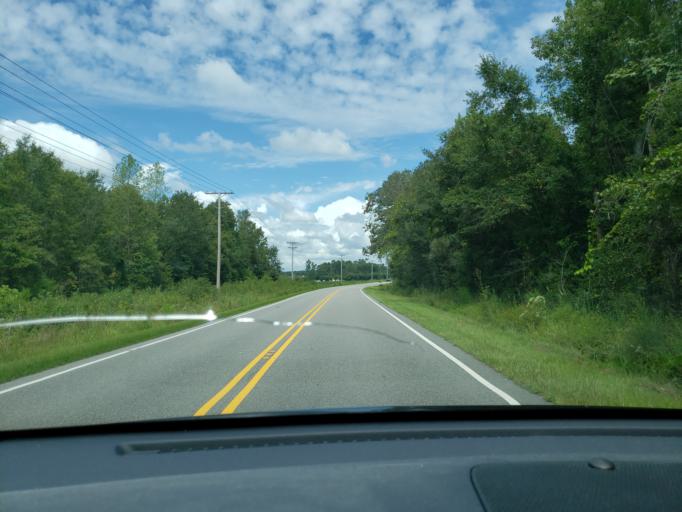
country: US
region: North Carolina
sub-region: Columbus County
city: Tabor City
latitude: 34.1709
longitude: -78.7843
